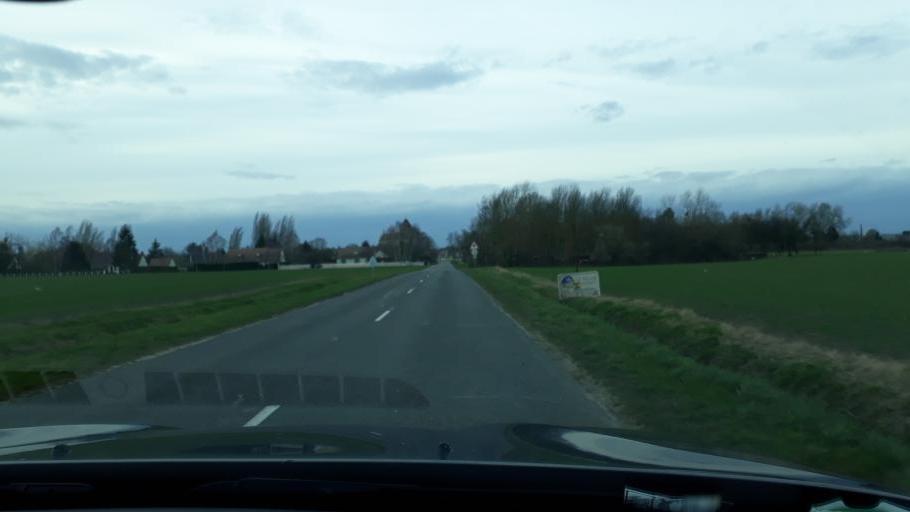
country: FR
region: Centre
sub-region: Departement du Loiret
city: Chilleurs-aux-Bois
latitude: 48.0692
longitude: 2.1418
